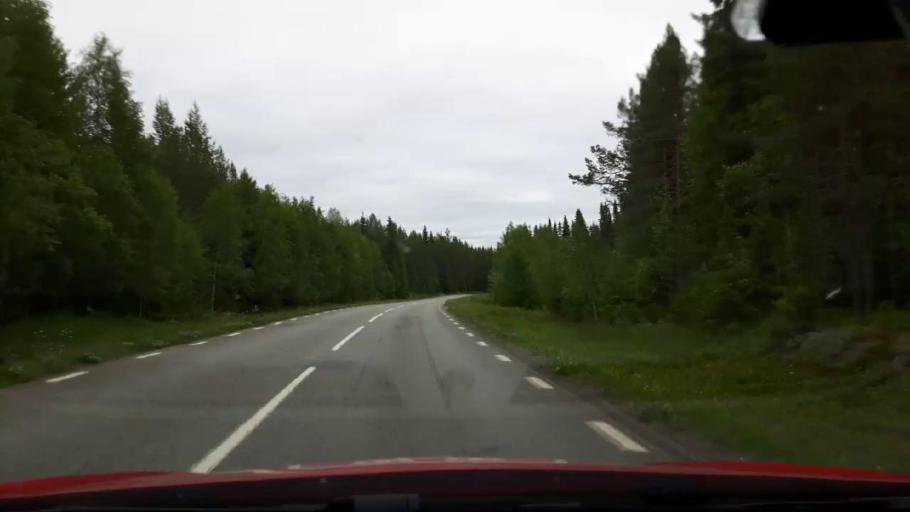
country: SE
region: Jaemtland
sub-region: Stroemsunds Kommun
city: Stroemsund
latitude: 63.4527
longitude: 15.4653
